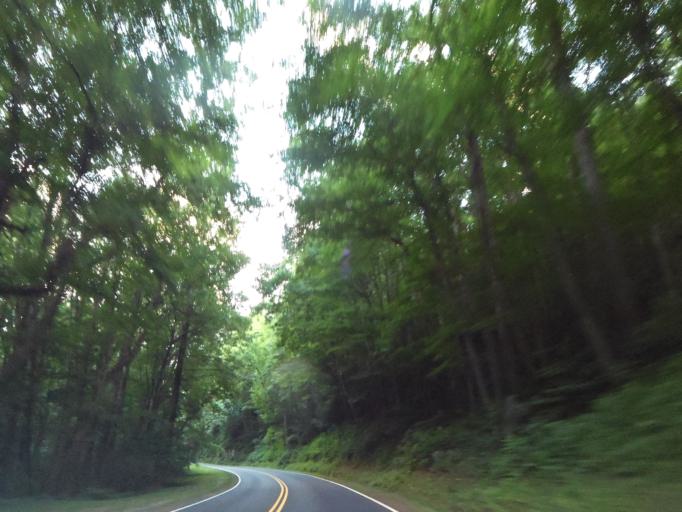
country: US
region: Tennessee
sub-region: Sevier County
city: Gatlinburg
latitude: 35.6454
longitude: -83.5099
